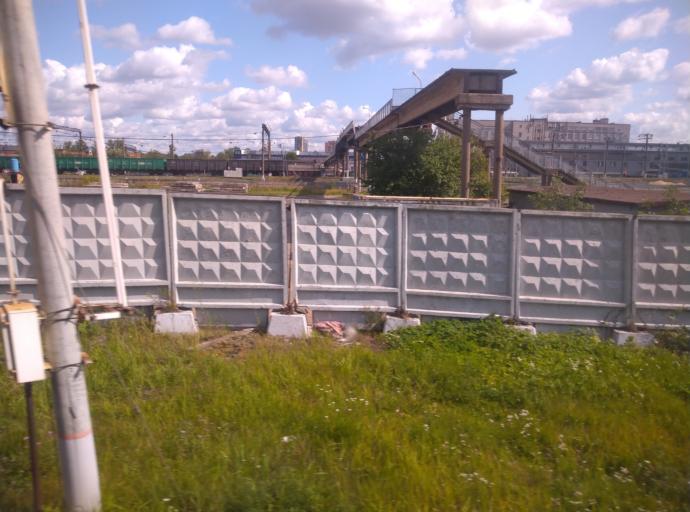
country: RU
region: St.-Petersburg
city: Obukhovo
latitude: 59.8781
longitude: 30.4091
